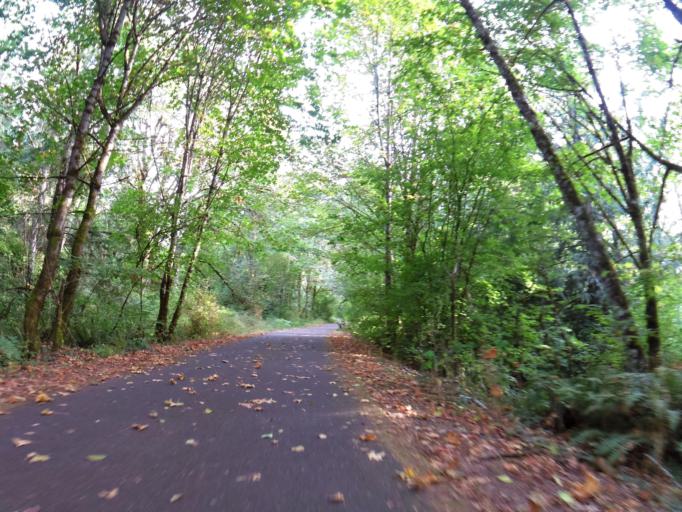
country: US
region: Washington
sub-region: Thurston County
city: Lacey
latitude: 46.9770
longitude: -122.8129
